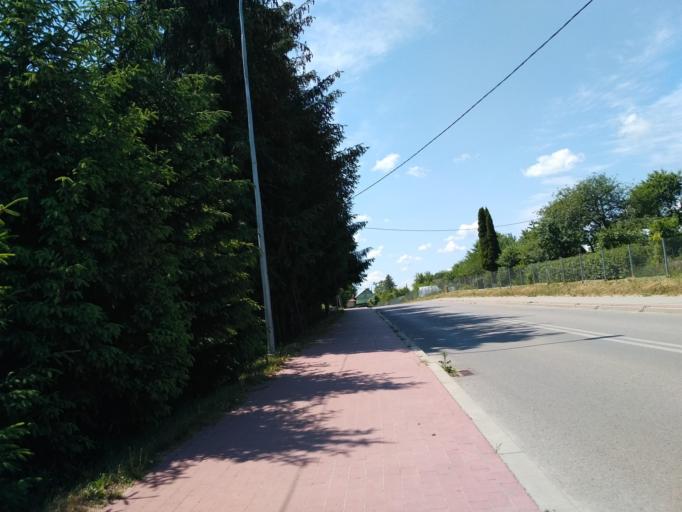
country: PL
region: Subcarpathian Voivodeship
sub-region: Krosno
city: Krosno
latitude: 49.7021
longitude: 21.7767
